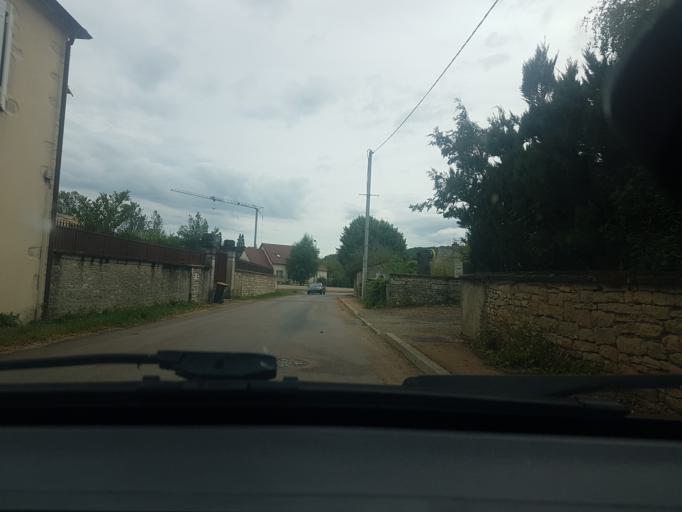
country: FR
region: Bourgogne
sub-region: Departement de Saone-et-Loire
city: Fontaines
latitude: 46.8609
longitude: 4.7602
